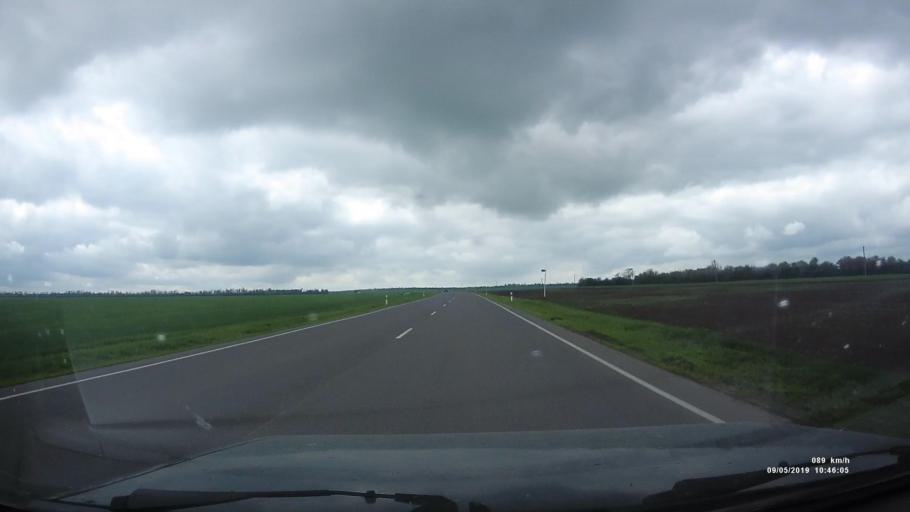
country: RU
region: Rostov
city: Peshkovo
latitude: 46.9893
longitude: 39.3593
